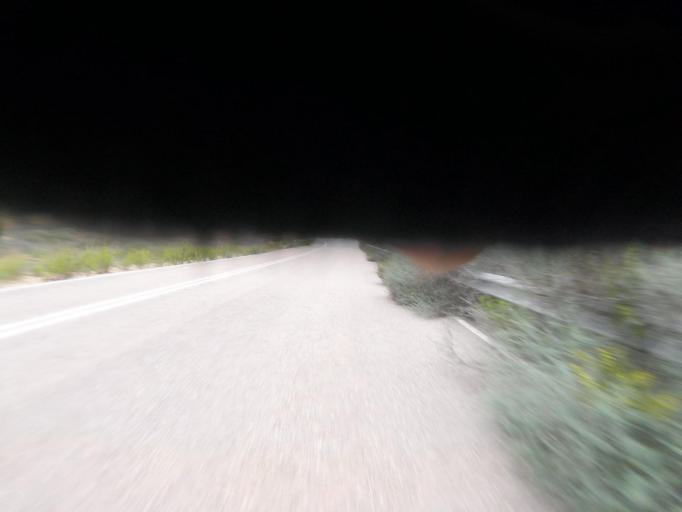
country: ES
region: Valencia
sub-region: Provincia de Castello
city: Benlloch
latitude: 40.1950
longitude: 0.0526
